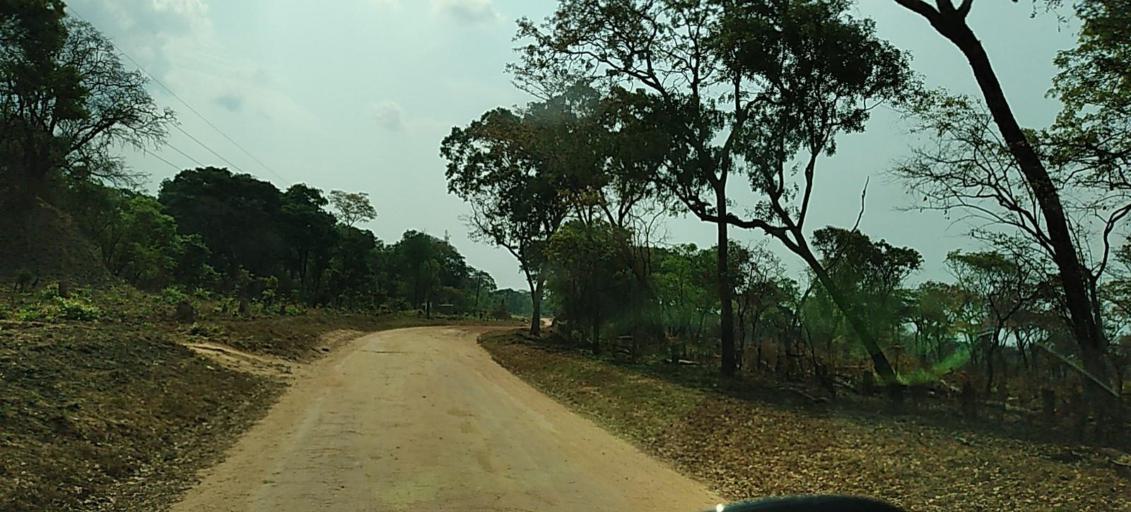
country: ZM
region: North-Western
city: Solwezi
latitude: -12.7097
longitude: 26.4222
